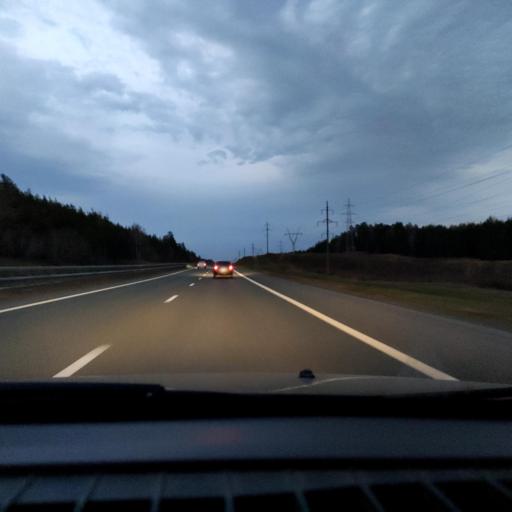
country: RU
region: Samara
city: Povolzhskiy
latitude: 53.5166
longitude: 49.7418
